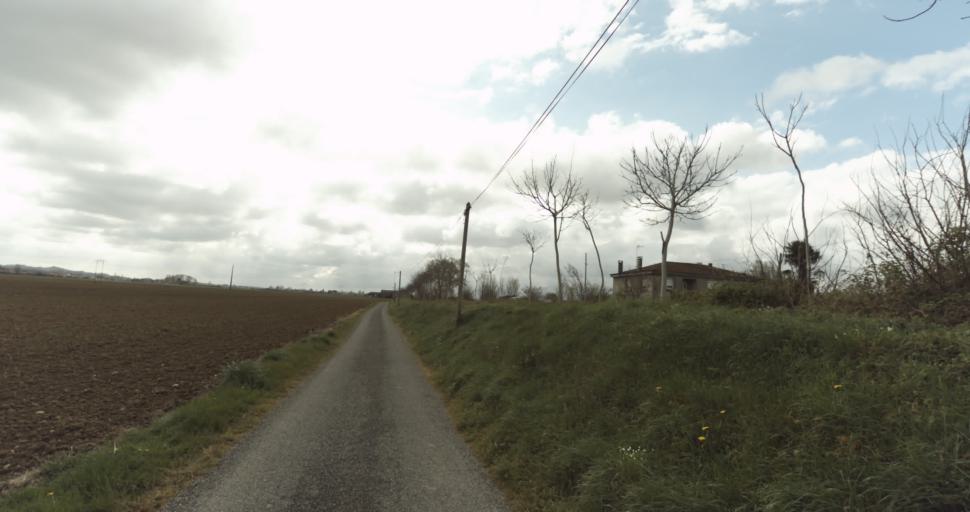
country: FR
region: Midi-Pyrenees
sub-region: Departement de la Haute-Garonne
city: Auterive
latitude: 43.3458
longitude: 1.4452
